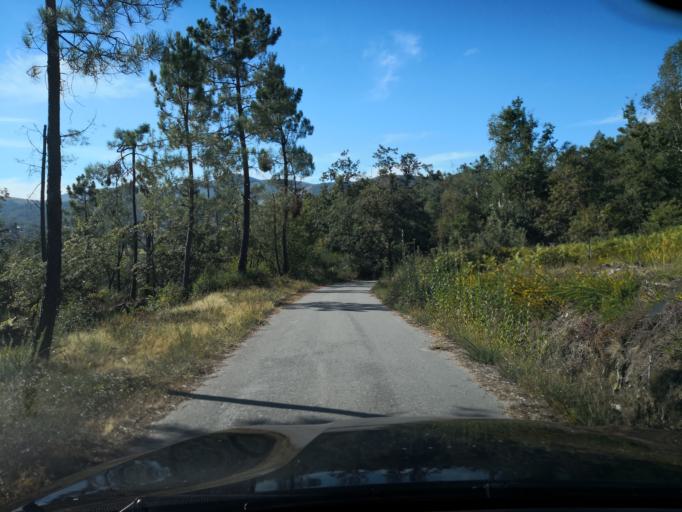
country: PT
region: Vila Real
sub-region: Santa Marta de Penaguiao
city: Santa Marta de Penaguiao
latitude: 41.2930
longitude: -7.8643
